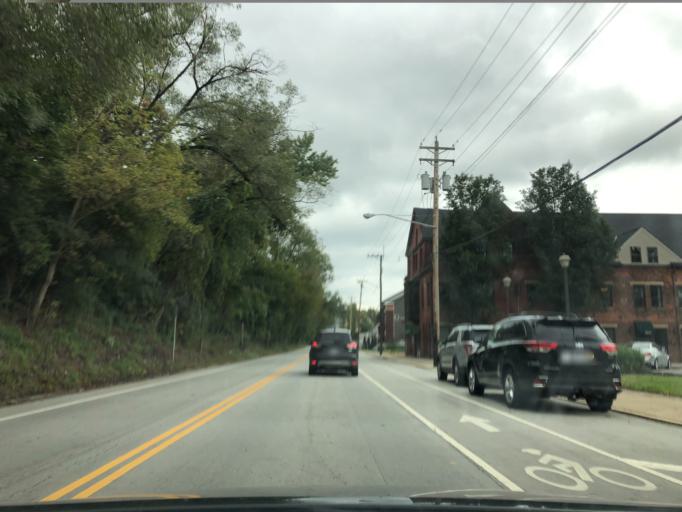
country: US
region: Kentucky
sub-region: Campbell County
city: Dayton
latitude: 39.1213
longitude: -84.4496
